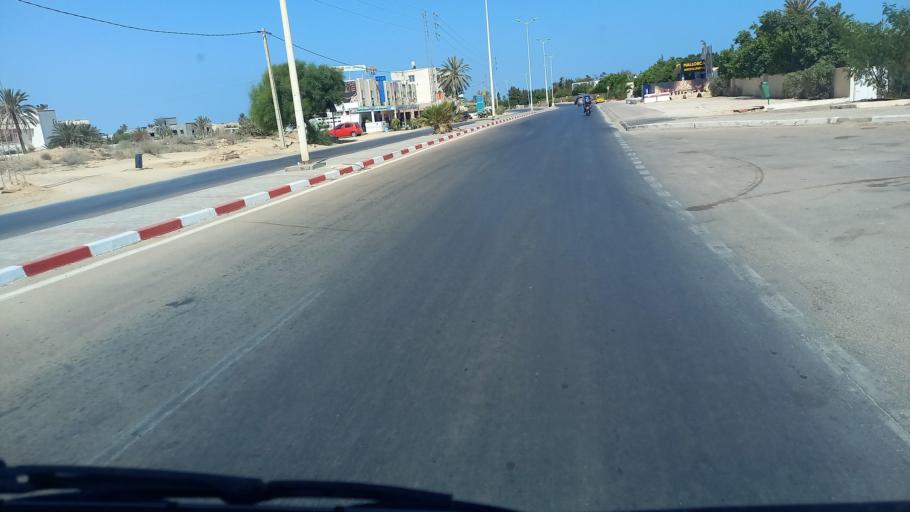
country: TN
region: Madanin
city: Midoun
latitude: 33.8579
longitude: 10.9755
